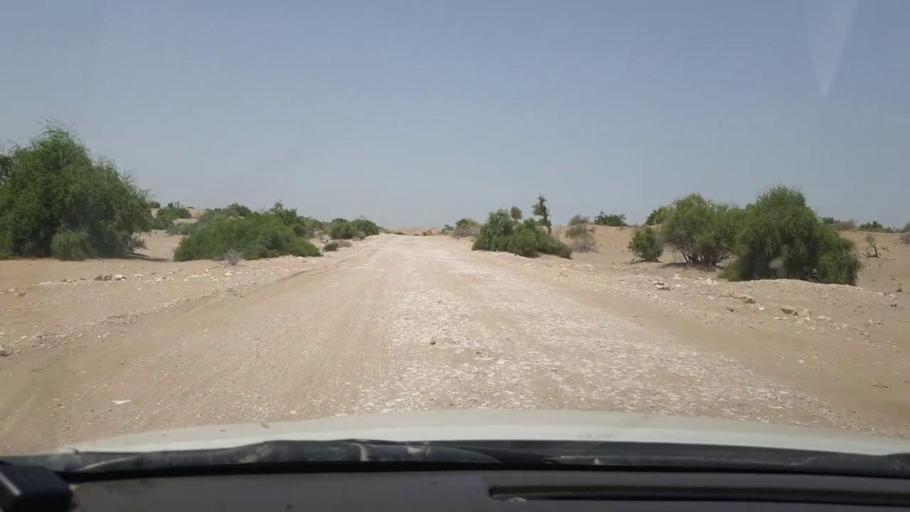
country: PK
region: Sindh
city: Rohri
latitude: 27.2878
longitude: 69.2407
